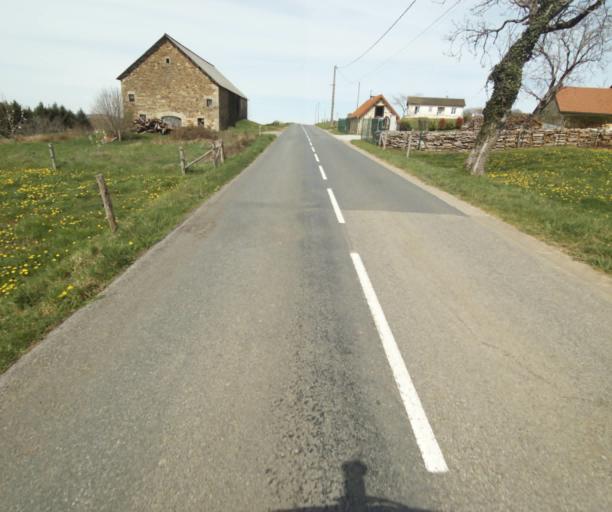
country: FR
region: Limousin
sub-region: Departement de la Correze
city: Naves
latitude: 45.3638
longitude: 1.7953
